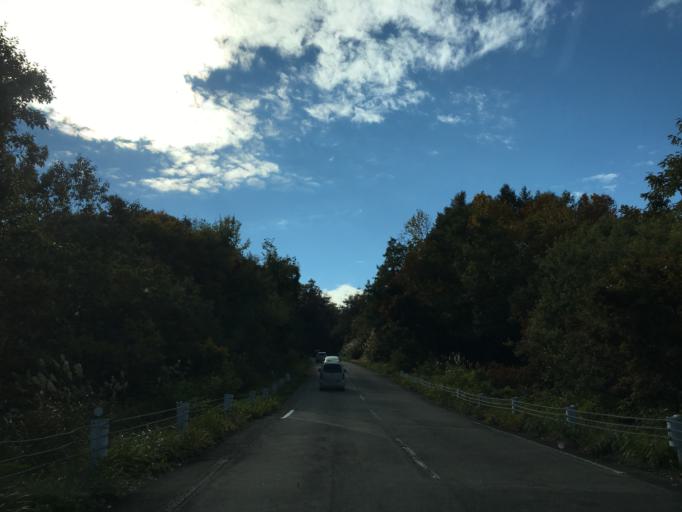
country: JP
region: Fukushima
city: Inawashiro
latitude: 37.6759
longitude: 140.1301
